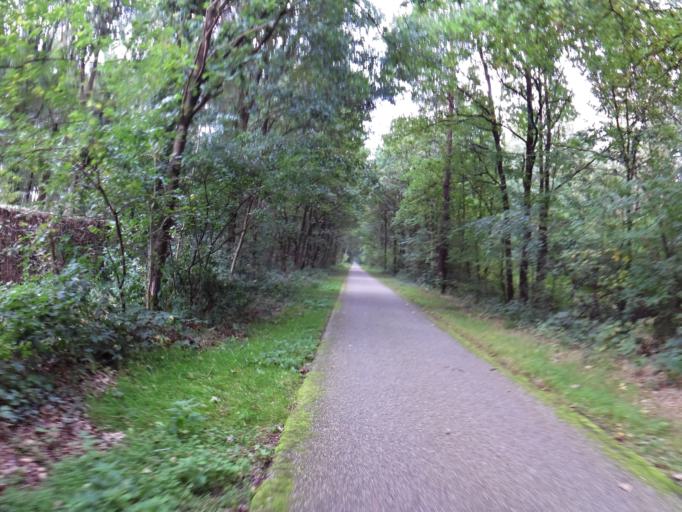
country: BE
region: Flanders
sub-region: Provincie Limburg
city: As
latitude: 51.0132
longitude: 5.6180
